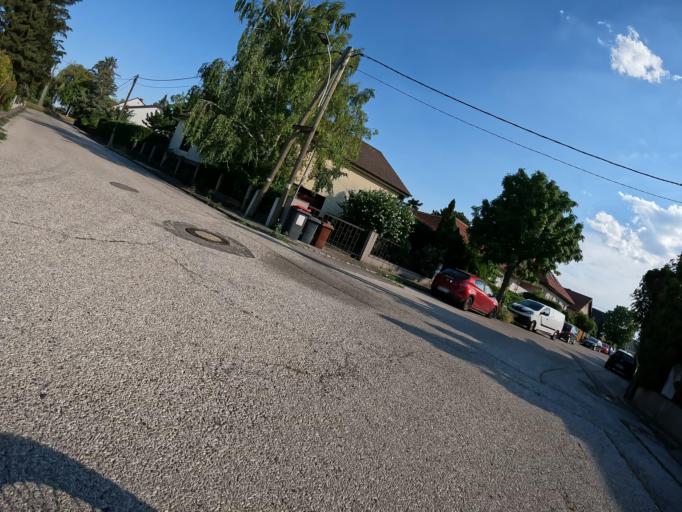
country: AT
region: Lower Austria
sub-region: Politischer Bezirk Modling
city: Guntramsdorf
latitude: 48.0394
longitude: 16.3131
